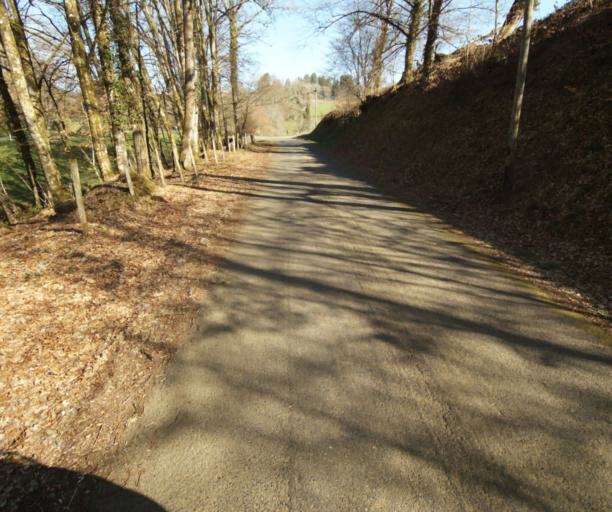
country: FR
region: Limousin
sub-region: Departement de la Correze
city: Seilhac
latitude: 45.3814
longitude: 1.7712
